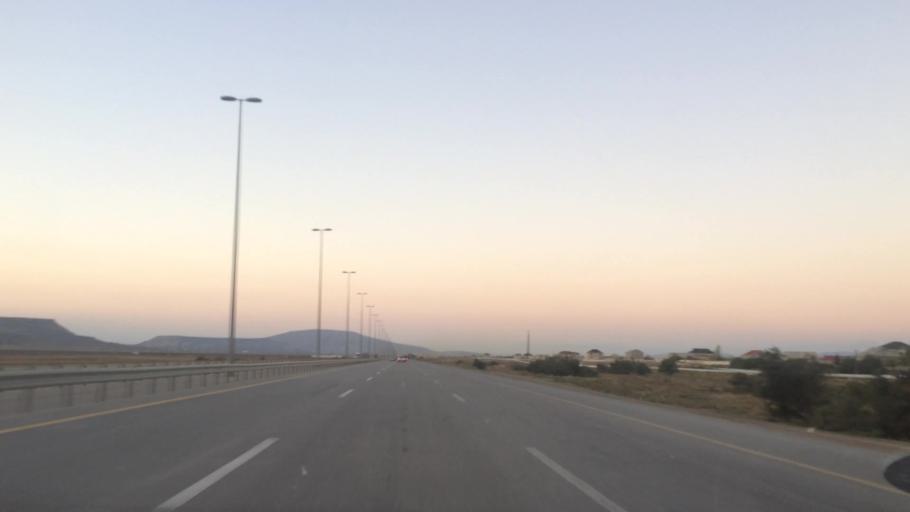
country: AZ
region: Baki
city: Qobustan
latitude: 40.0261
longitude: 49.4238
